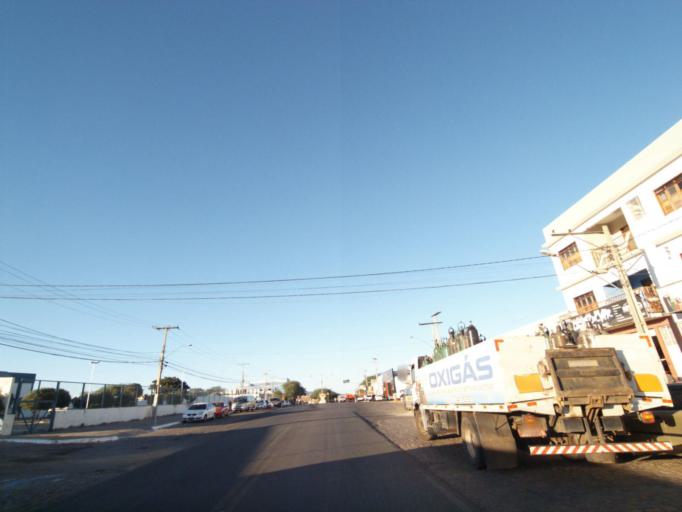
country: BR
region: Bahia
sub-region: Brumado
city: Brumado
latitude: -14.2150
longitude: -41.6795
